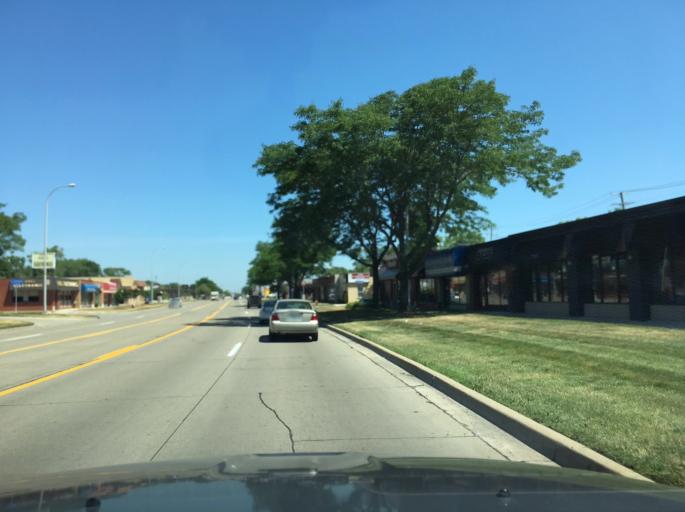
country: US
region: Michigan
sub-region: Macomb County
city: Saint Clair Shores
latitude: 42.4906
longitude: -82.8971
